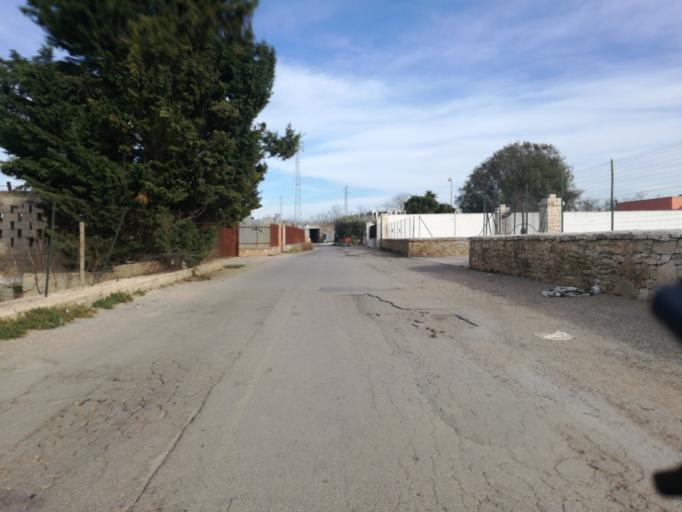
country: IT
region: Apulia
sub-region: Provincia di Bari
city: Capurso
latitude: 41.0495
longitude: 16.9087
